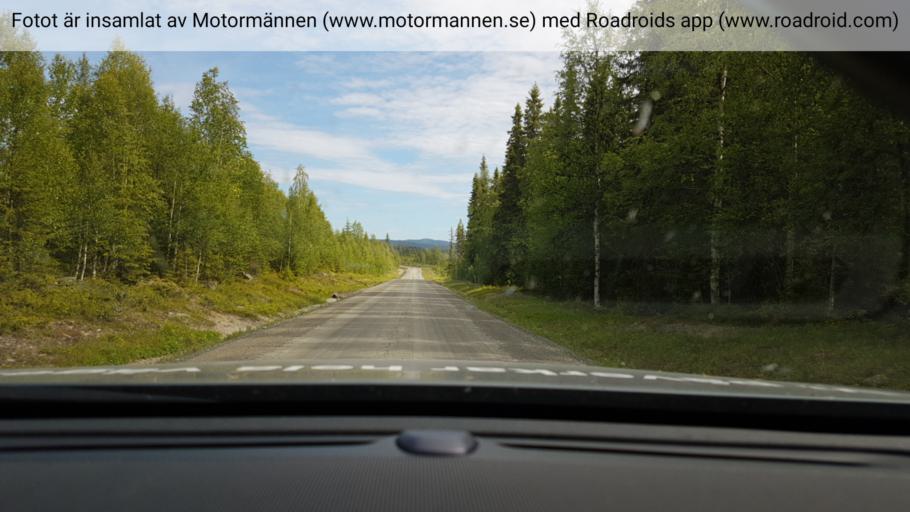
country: SE
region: Vaesterbotten
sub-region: Storumans Kommun
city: Fristad
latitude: 65.1802
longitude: 16.4059
